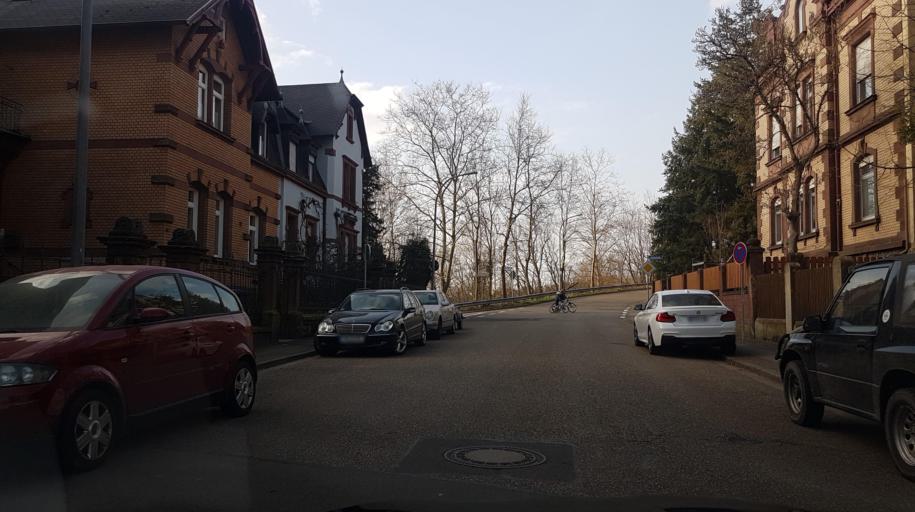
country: DE
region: Rheinland-Pfalz
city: Pirmasens
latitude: 49.2065
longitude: 7.5999
